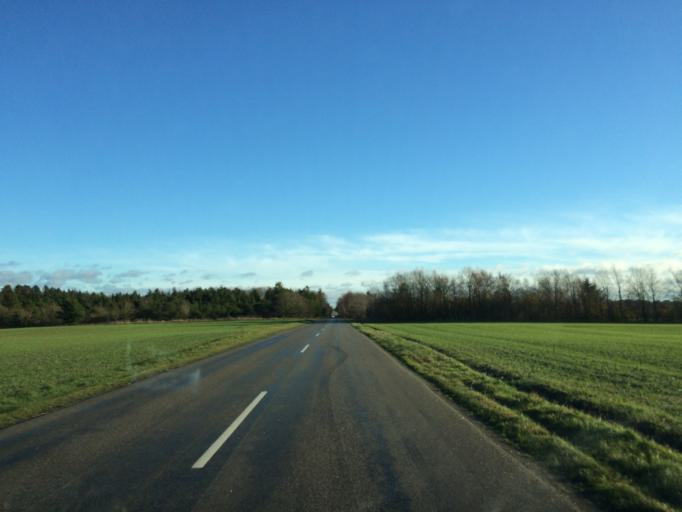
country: DK
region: Central Jutland
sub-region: Herning Kommune
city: Kibaek
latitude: 56.0688
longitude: 8.7483
